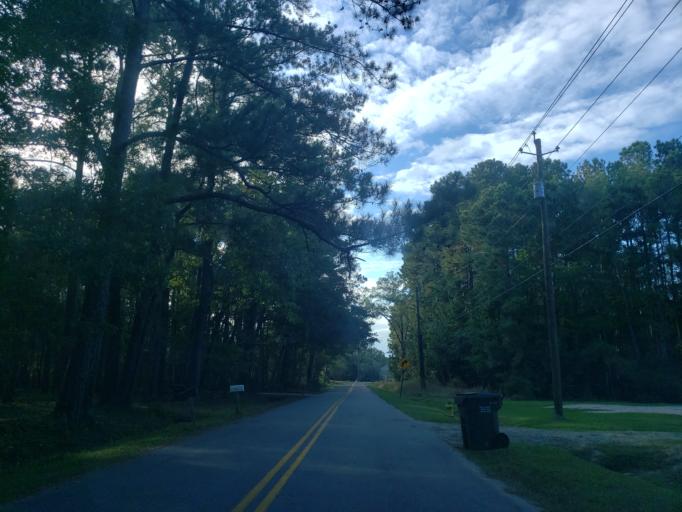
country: US
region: Georgia
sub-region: Chatham County
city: Georgetown
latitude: 31.9952
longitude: -81.2409
